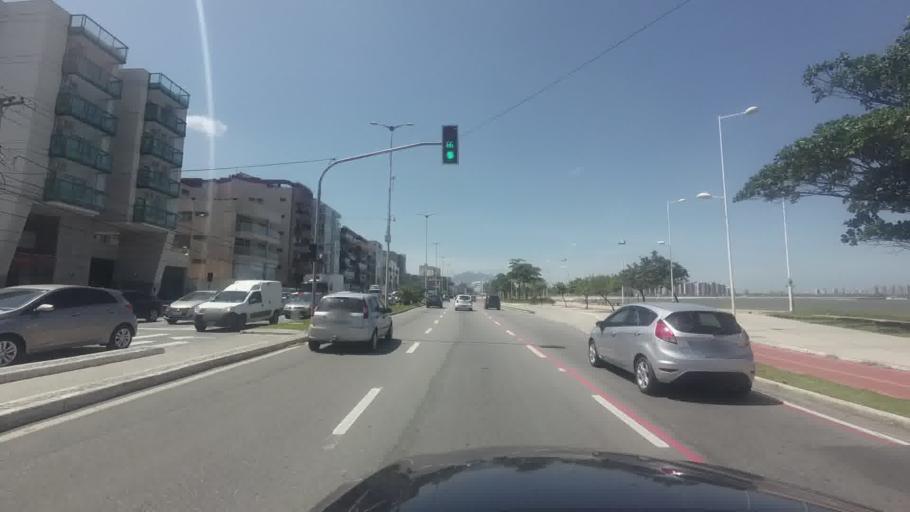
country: BR
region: Espirito Santo
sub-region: Vila Velha
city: Vila Velha
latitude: -20.2907
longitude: -40.2903
